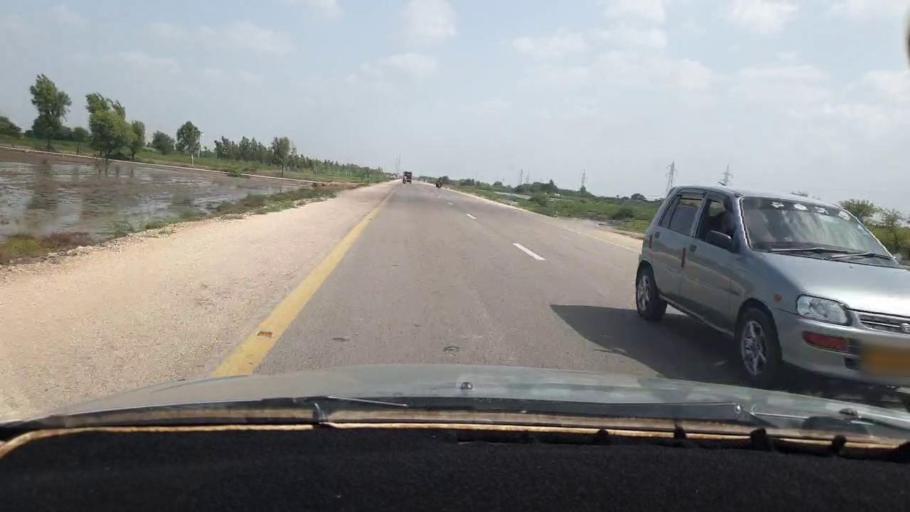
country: PK
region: Sindh
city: Digri
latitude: 25.0380
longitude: 69.2375
